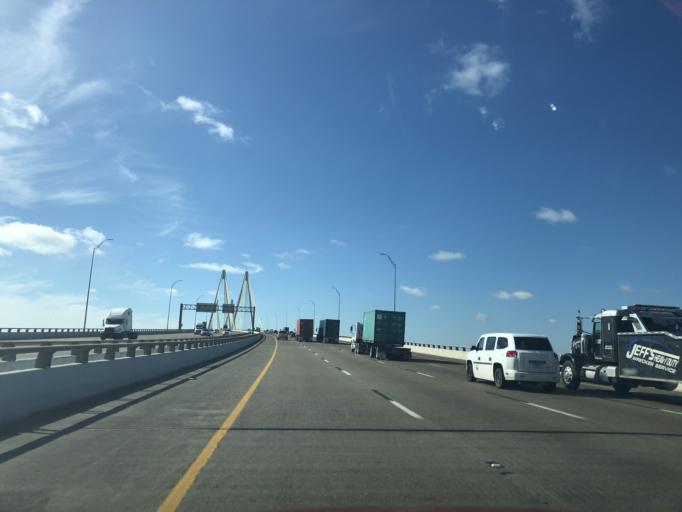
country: US
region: Texas
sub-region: Harris County
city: Baytown
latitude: 29.7095
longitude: -95.0095
